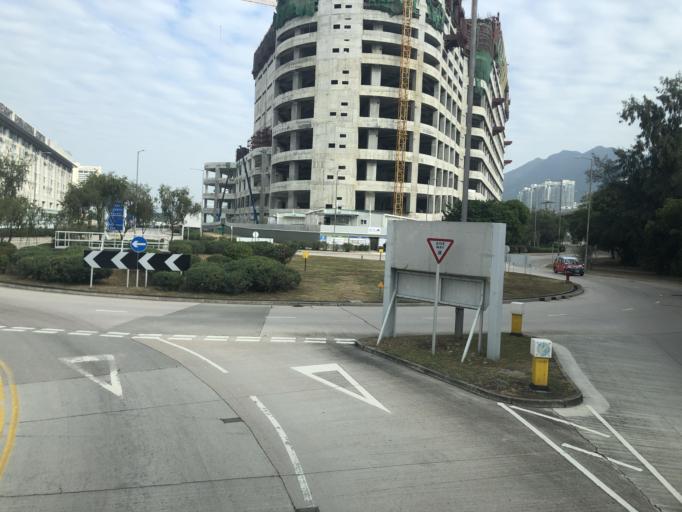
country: HK
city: Tai O
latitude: 22.2932
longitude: 113.9249
